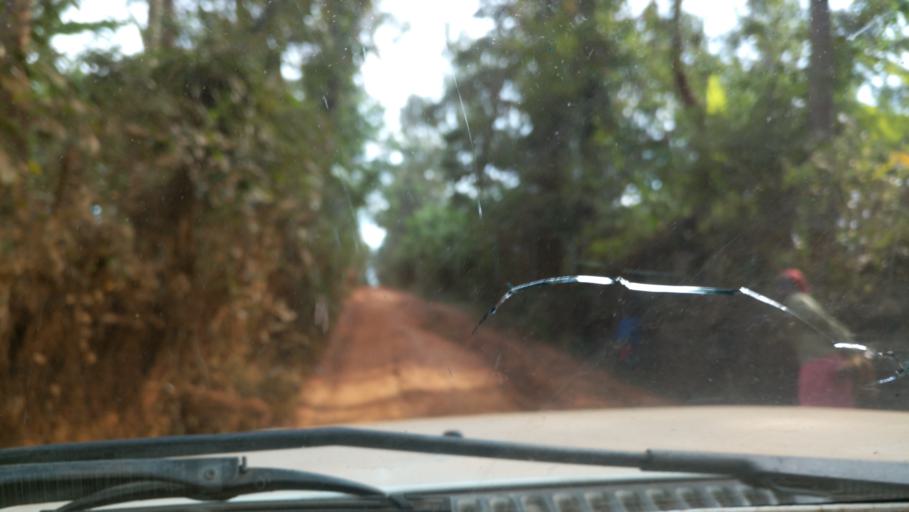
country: KE
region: Murang'a District
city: Maragua
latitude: -0.7780
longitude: 37.1064
